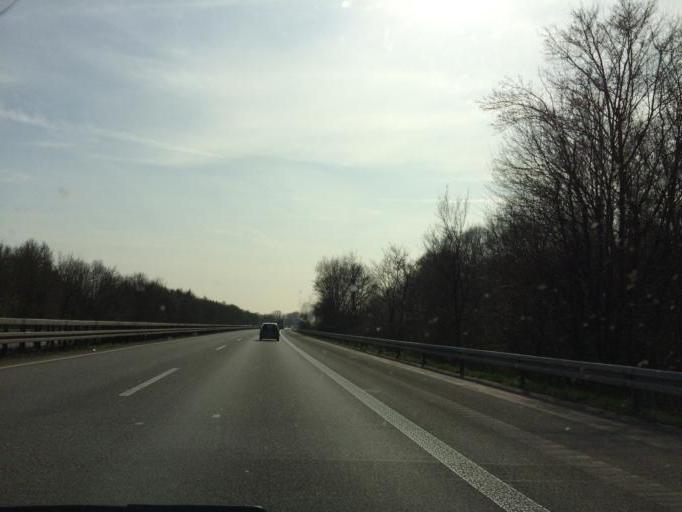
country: DE
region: North Rhine-Westphalia
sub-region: Regierungsbezirk Munster
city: Dulmen
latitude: 51.8301
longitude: 7.2362
